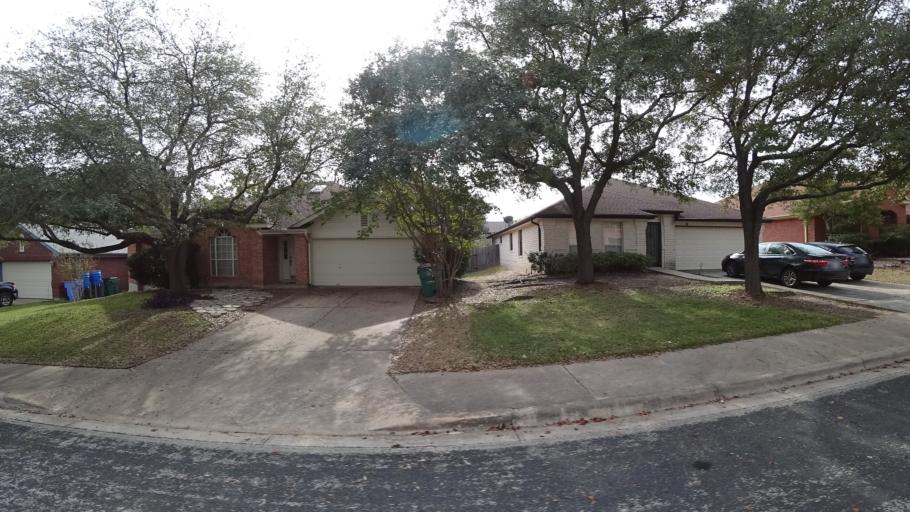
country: US
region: Texas
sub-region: Travis County
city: Wells Branch
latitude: 30.4504
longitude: -97.6756
